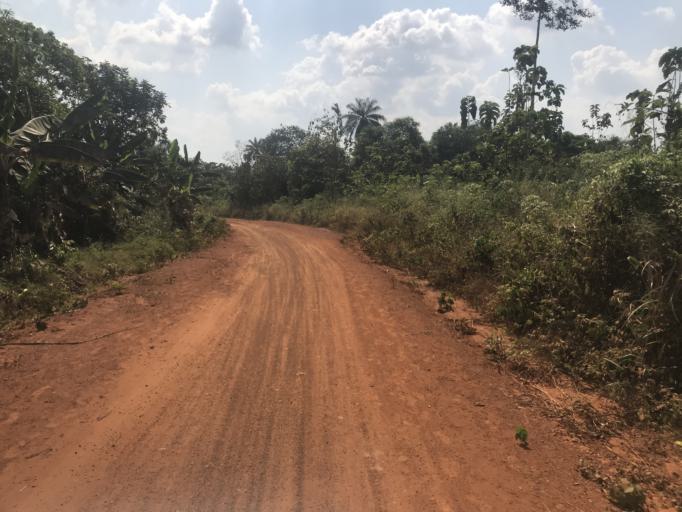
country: NG
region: Osun
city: Ibokun
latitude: 7.8043
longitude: 4.6883
